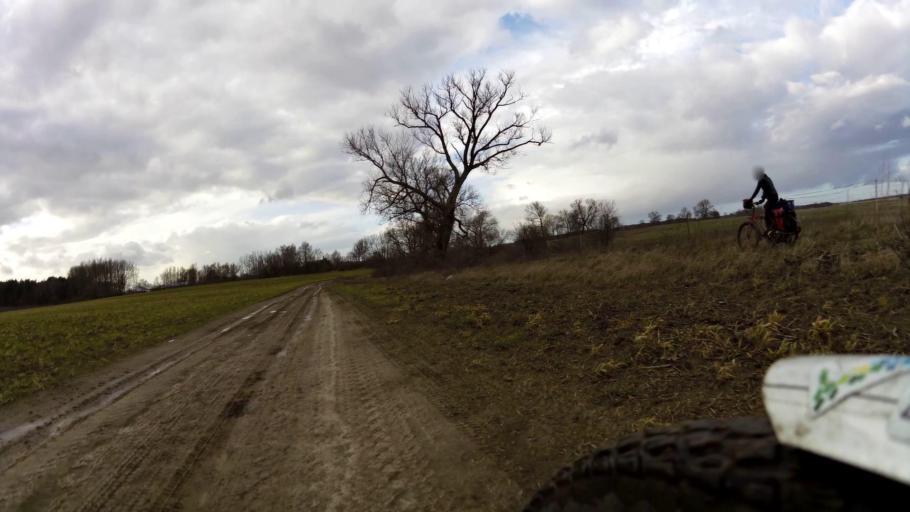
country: PL
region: West Pomeranian Voivodeship
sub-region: Powiat kamienski
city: Wolin
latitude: 53.8733
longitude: 14.7101
